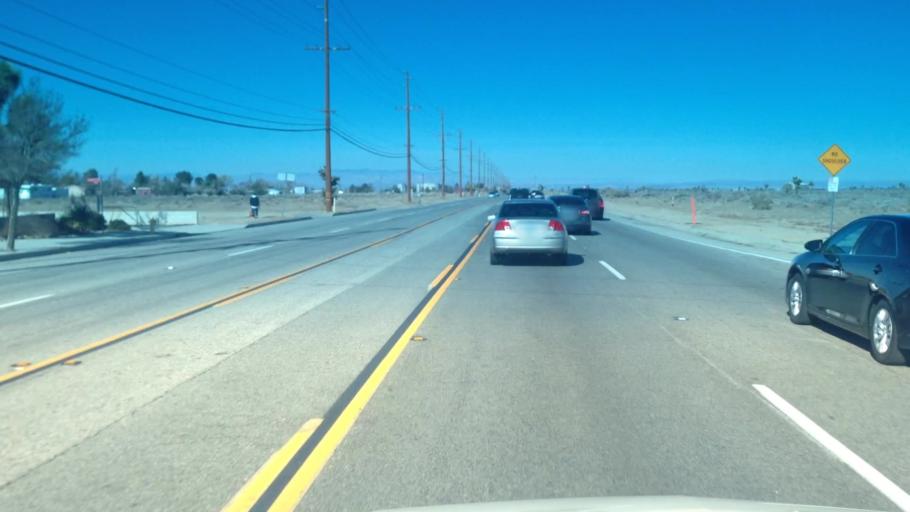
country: US
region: California
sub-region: Los Angeles County
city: Desert View Highlands
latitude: 34.6175
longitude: -118.1477
